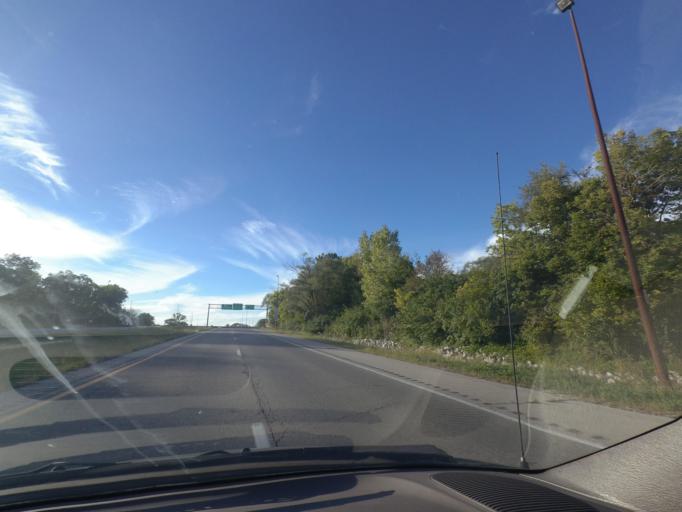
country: US
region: Illinois
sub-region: Sangamon County
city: Grandview
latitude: 39.7837
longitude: -89.5950
